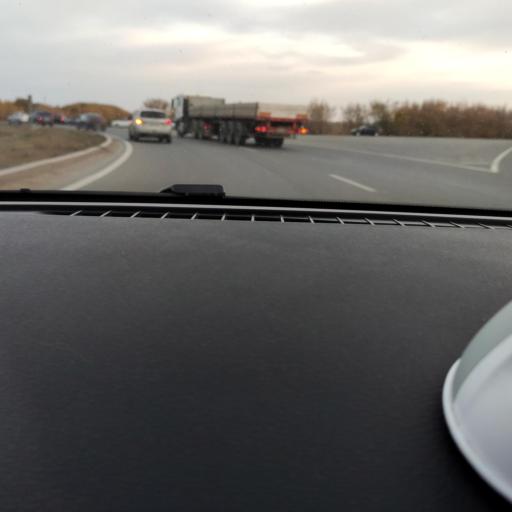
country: RU
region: Samara
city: Samara
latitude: 53.0916
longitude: 50.1499
